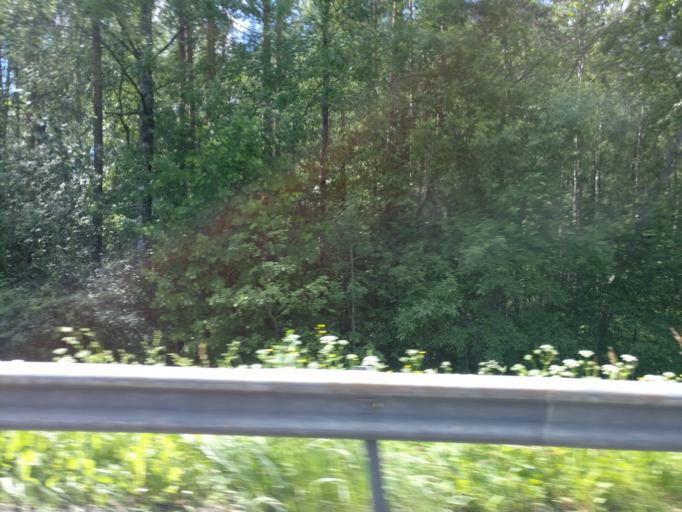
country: FI
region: Southern Savonia
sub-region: Savonlinna
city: Kerimaeki
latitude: 61.8709
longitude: 29.1247
